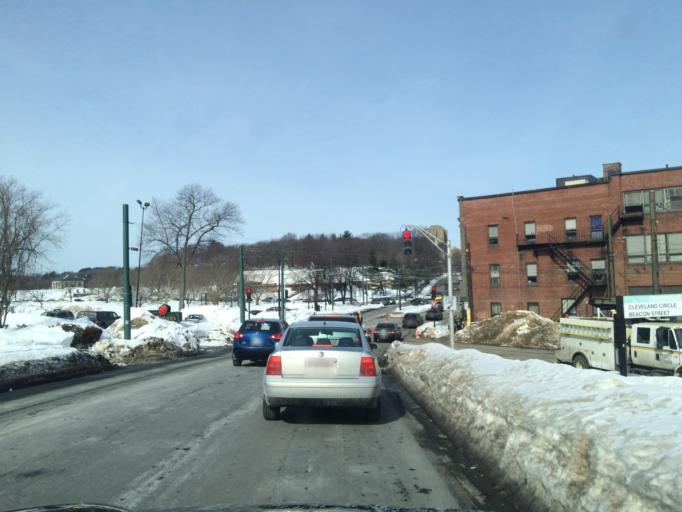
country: US
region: Massachusetts
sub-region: Norfolk County
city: Brookline
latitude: 42.3351
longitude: -71.1497
